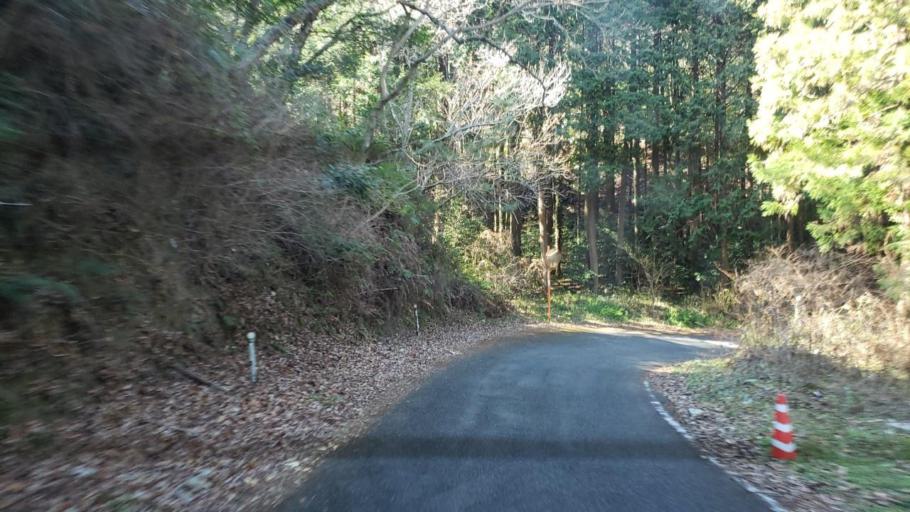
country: JP
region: Tokushima
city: Narutocho-mitsuishi
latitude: 34.1988
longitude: 134.5538
